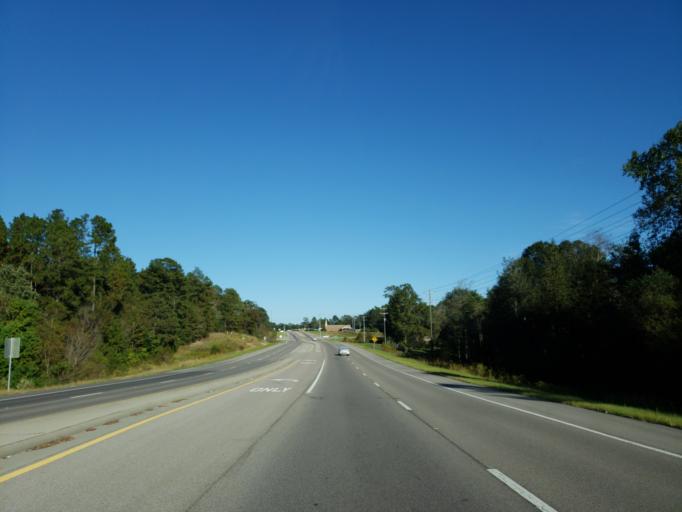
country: US
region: Mississippi
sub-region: Forrest County
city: Petal
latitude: 31.3511
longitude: -89.1798
